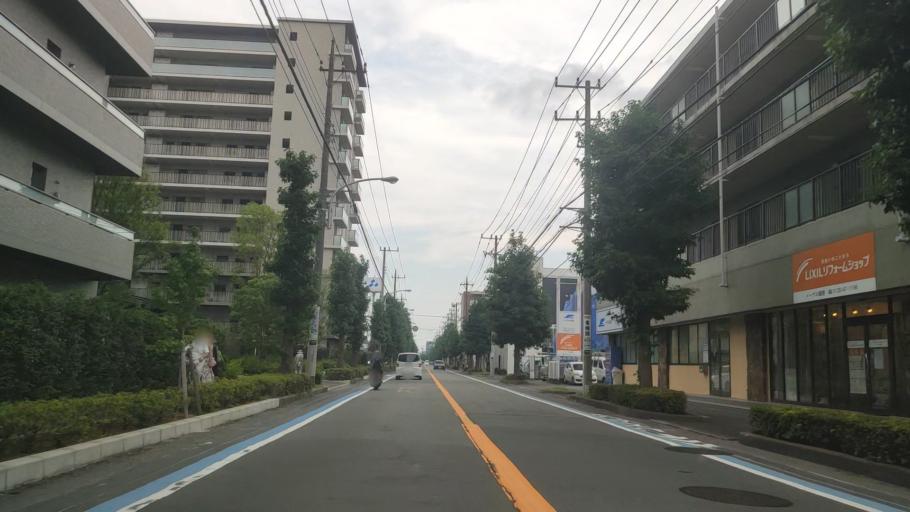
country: JP
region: Kanagawa
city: Minami-rinkan
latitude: 35.5066
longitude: 139.4487
